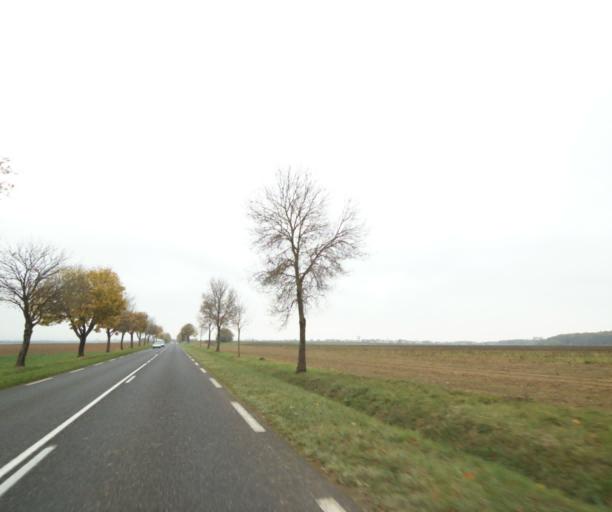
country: FR
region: Lorraine
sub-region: Departement de Meurthe-et-Moselle
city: Briey
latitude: 49.2655
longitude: 5.9515
